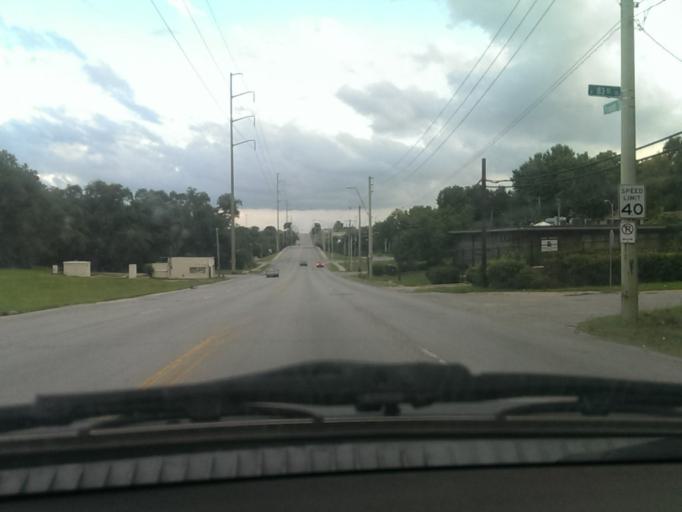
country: US
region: Kansas
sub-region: Johnson County
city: Leawood
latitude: 38.9769
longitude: -94.5764
